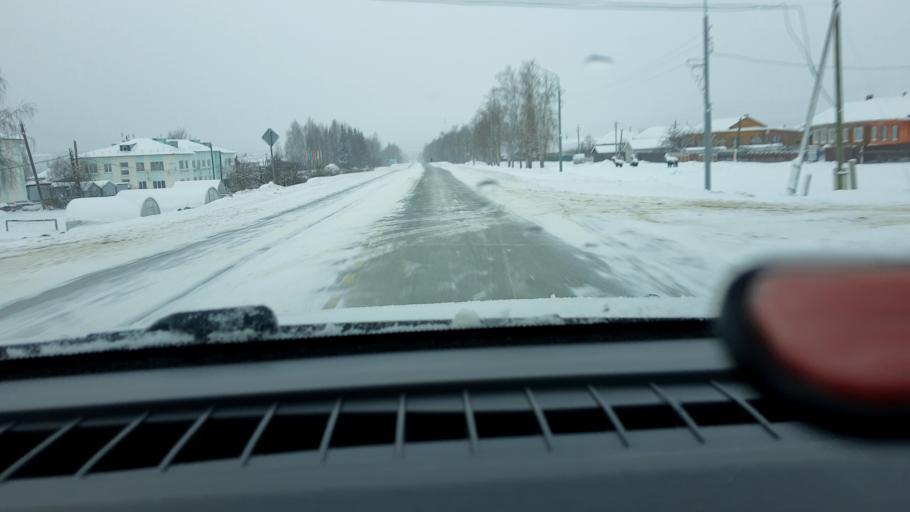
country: RU
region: Nizjnij Novgorod
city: Sharanga
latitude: 57.1854
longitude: 46.5336
